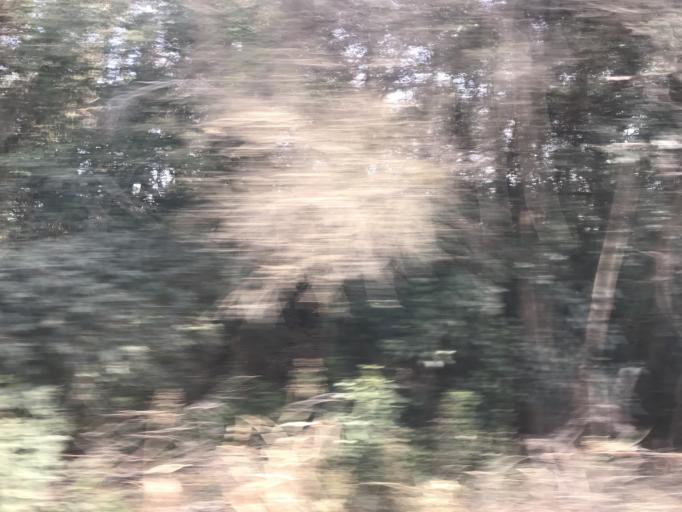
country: AR
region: Cordoba
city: Laguna Larga
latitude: -31.8026
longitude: -63.7804
